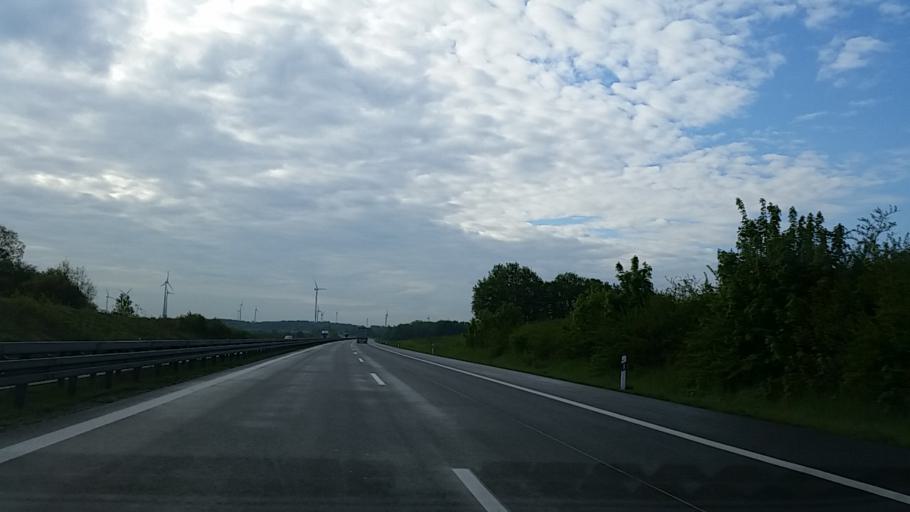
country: DE
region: Brandenburg
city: Gerdshagen
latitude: 53.2473
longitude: 12.1786
